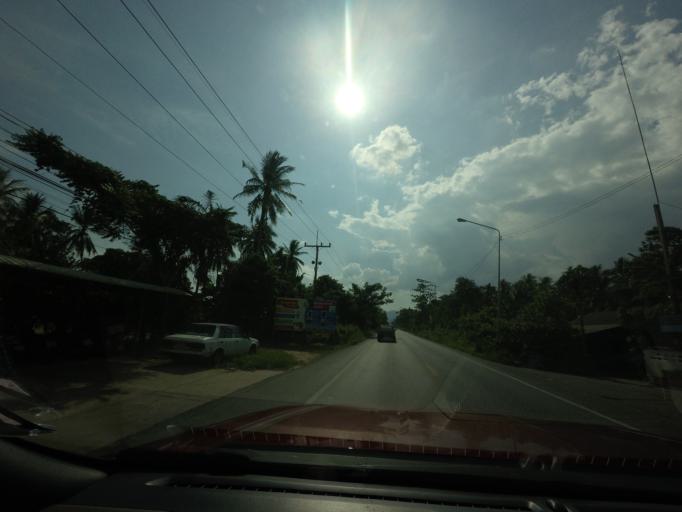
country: TH
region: Yala
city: Yala
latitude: 6.5616
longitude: 101.2167
